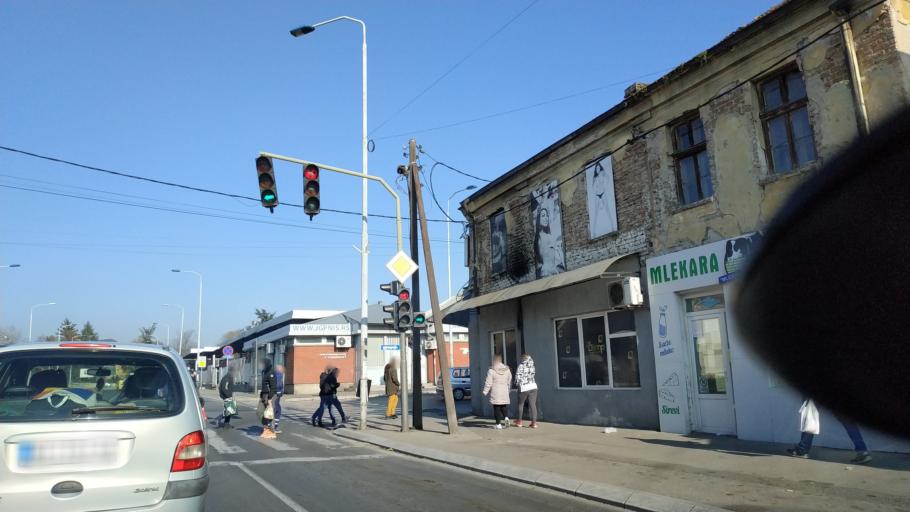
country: RS
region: Central Serbia
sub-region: Nisavski Okrug
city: Nis
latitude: 43.3242
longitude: 21.8902
